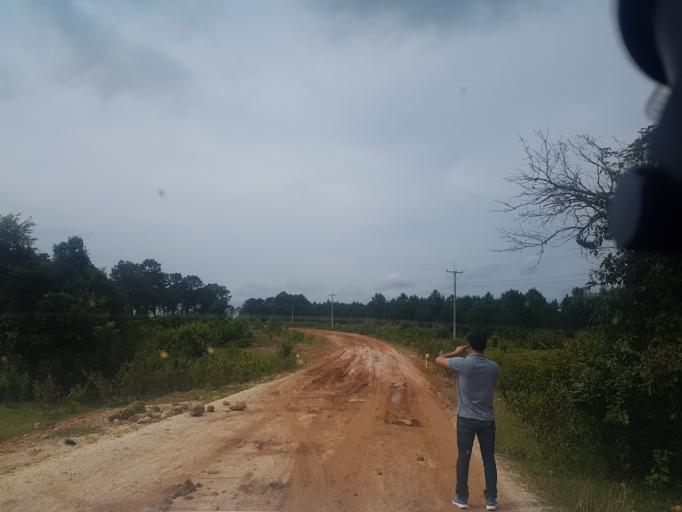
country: LA
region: Xiangkhoang
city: Phonsavan
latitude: 19.6192
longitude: 103.1241
